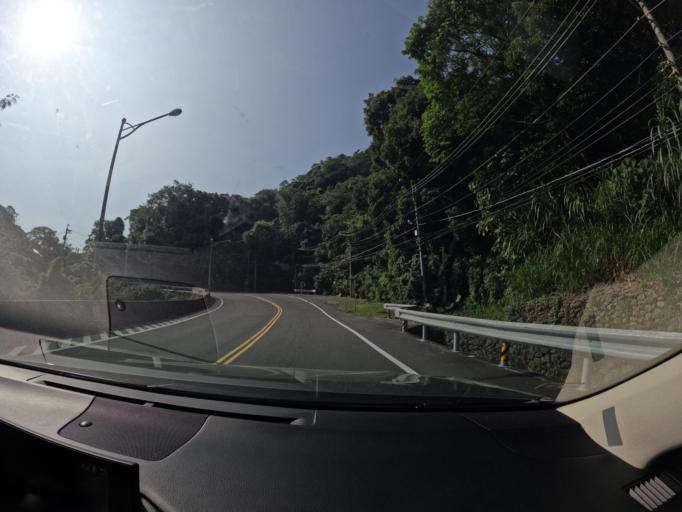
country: TW
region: Taiwan
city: Yujing
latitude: 23.0701
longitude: 120.5522
